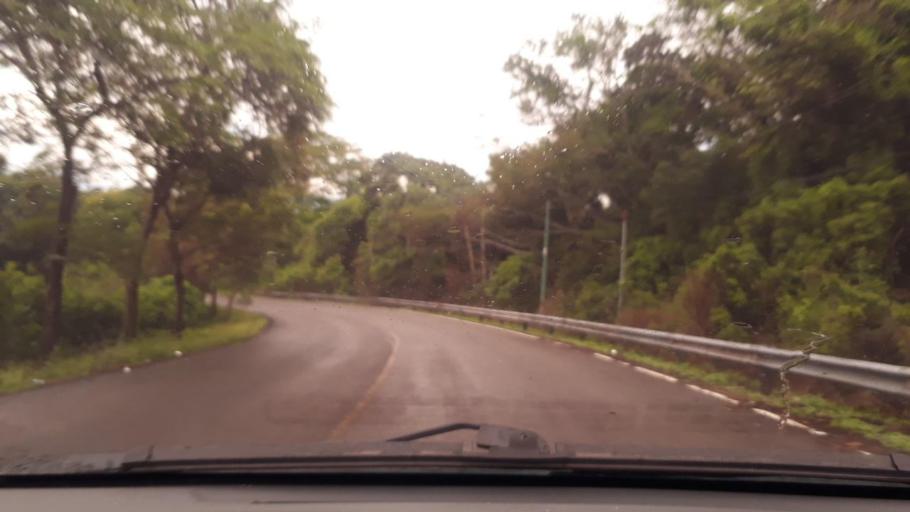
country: GT
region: Jutiapa
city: Comapa
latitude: 14.0332
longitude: -89.9120
